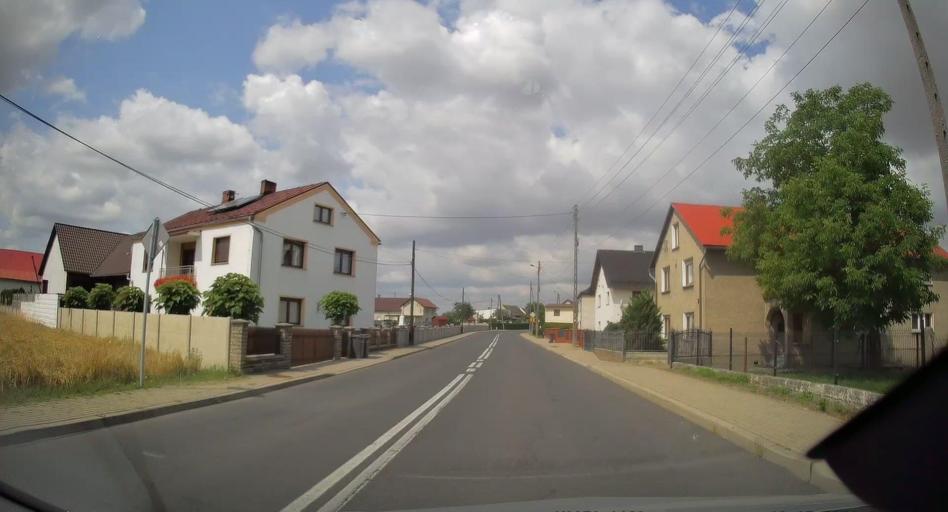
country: PL
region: Opole Voivodeship
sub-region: Powiat prudnicki
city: Twardawa
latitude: 50.3421
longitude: 17.9957
